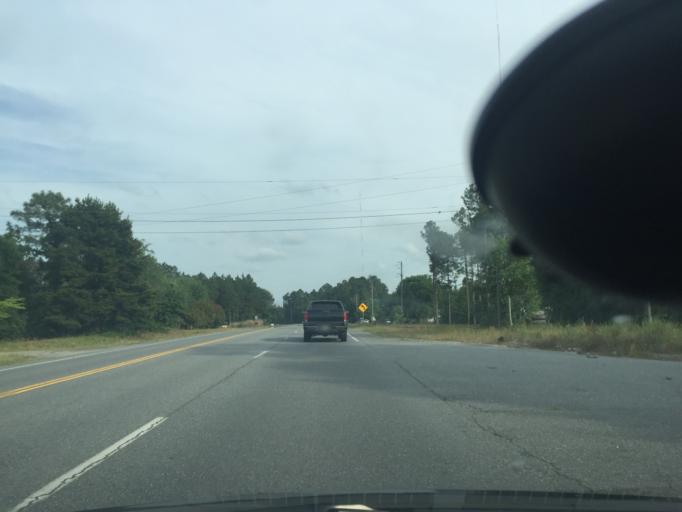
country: US
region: Georgia
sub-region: Chatham County
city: Bloomingdale
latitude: 32.0616
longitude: -81.3536
